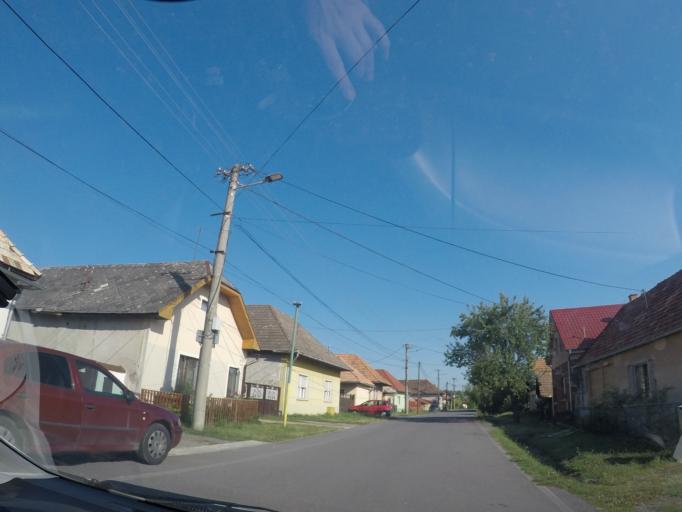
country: SK
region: Banskobystricky
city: Dudince
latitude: 48.1856
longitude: 18.8449
